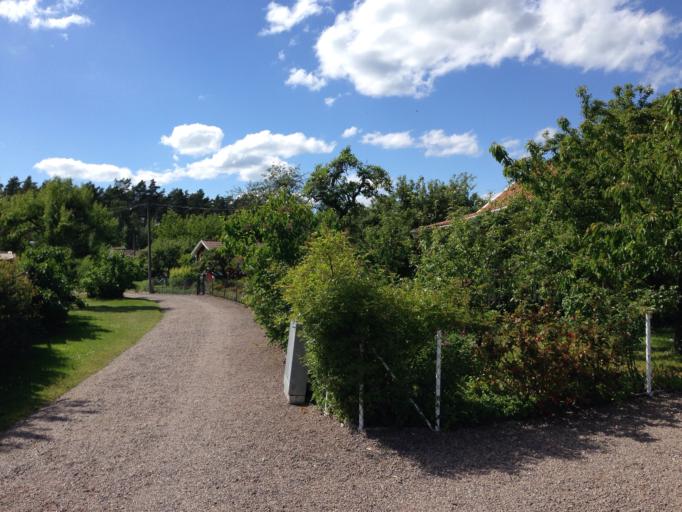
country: SE
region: Kalmar
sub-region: Kalmar Kommun
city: Kalmar
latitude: 56.6561
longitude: 16.3311
